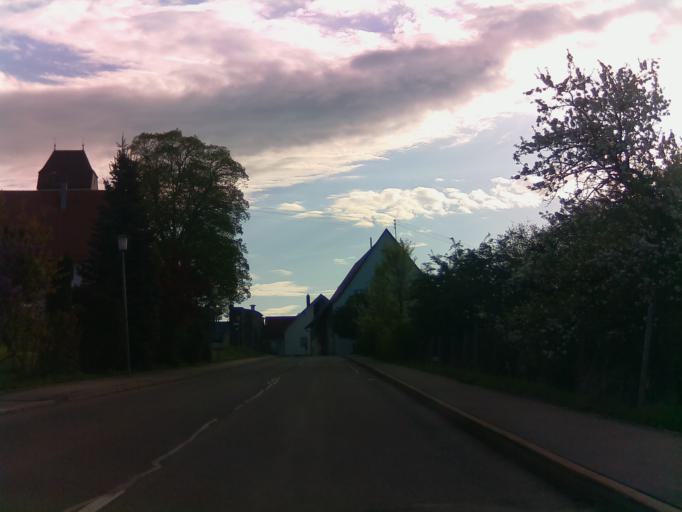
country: DE
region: Baden-Wuerttemberg
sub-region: Tuebingen Region
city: Rosenfeld
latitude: 48.2643
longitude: 8.7013
